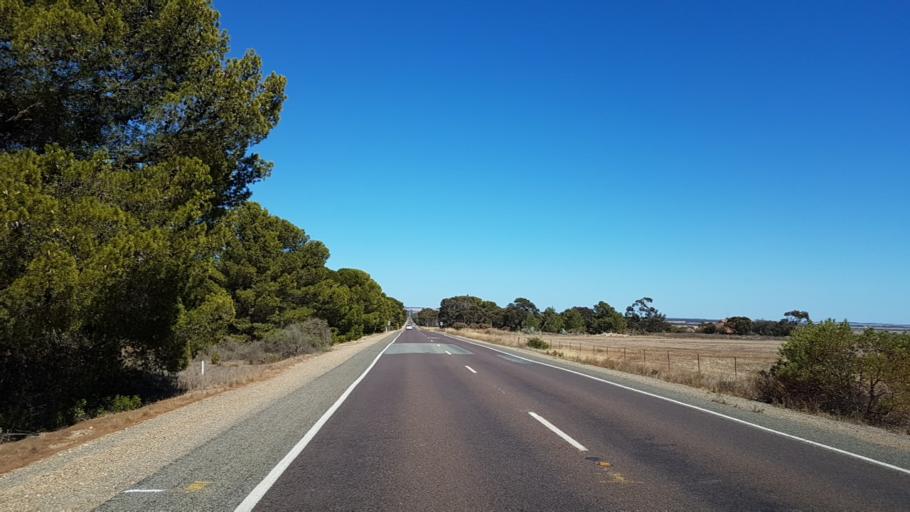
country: AU
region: South Australia
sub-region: Copper Coast
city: Kadina
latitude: -34.0586
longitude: 138.0303
